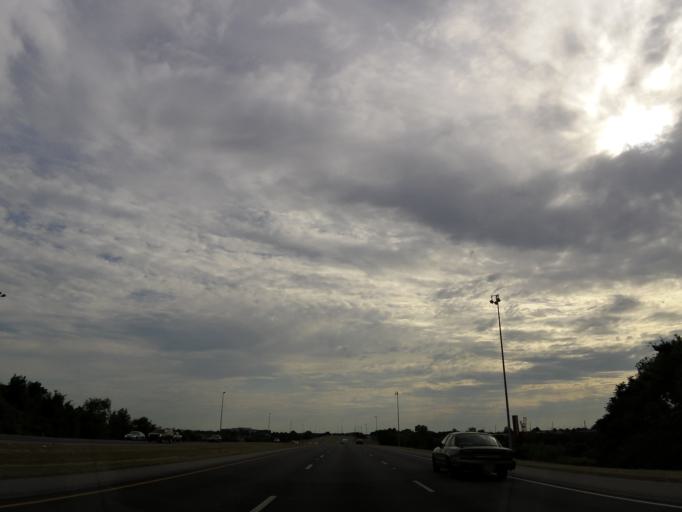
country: US
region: Alabama
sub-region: Madison County
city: Madison
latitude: 34.6831
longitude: -86.7307
